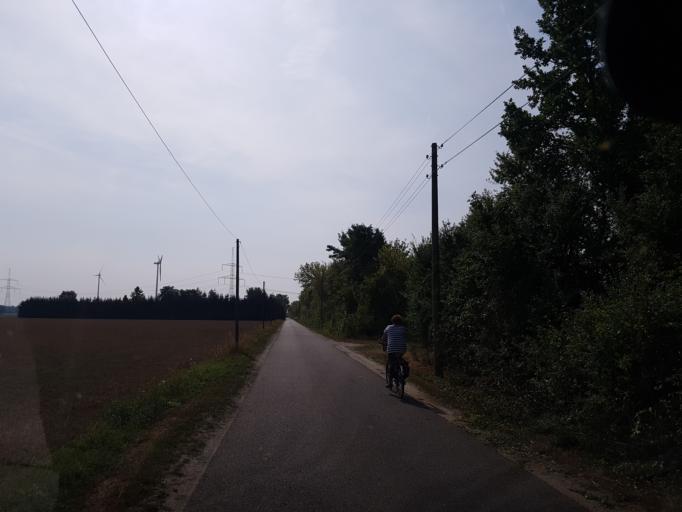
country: DE
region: Brandenburg
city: Finsterwalde
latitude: 51.6582
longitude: 13.7186
